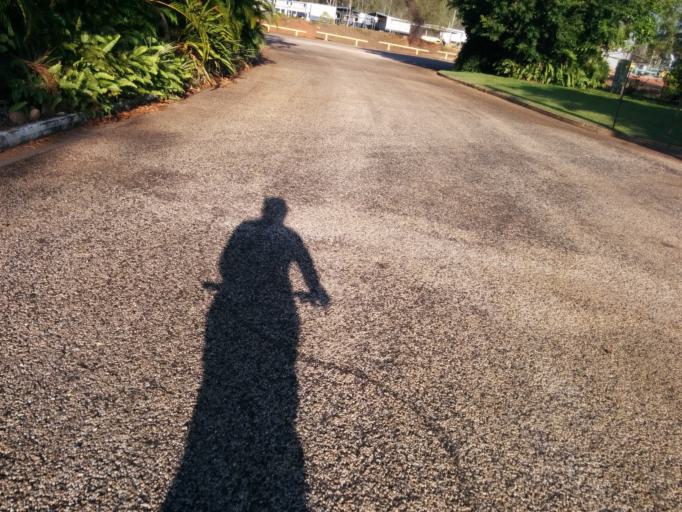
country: AU
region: Northern Territory
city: Alyangula
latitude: -13.8492
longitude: 136.4241
